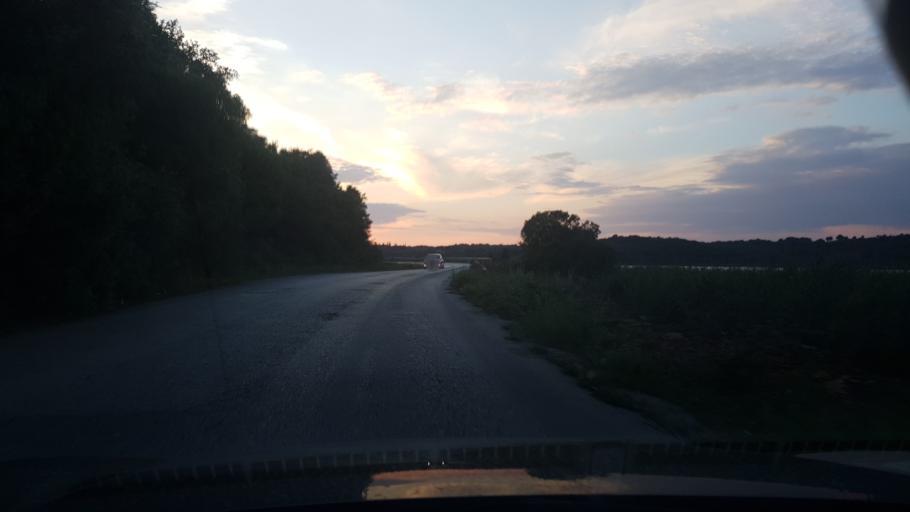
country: GR
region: West Greece
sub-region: Nomos Aitolias kai Akarnanias
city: Vonitsa
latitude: 38.9165
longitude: 20.8710
